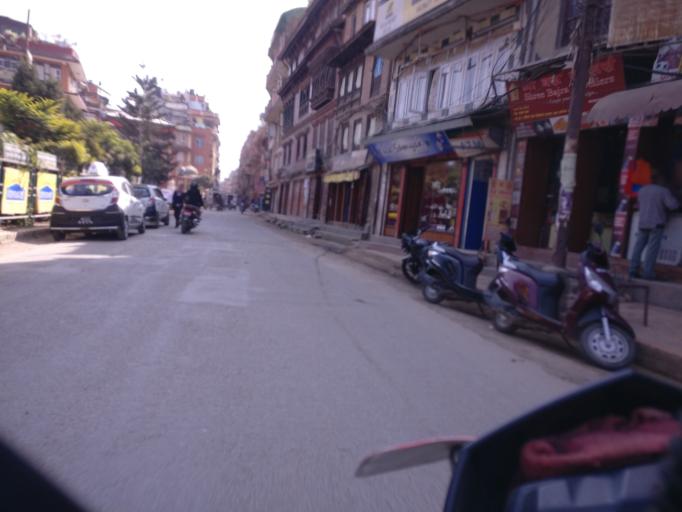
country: NP
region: Central Region
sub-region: Bagmati Zone
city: Patan
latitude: 27.6721
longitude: 85.3254
